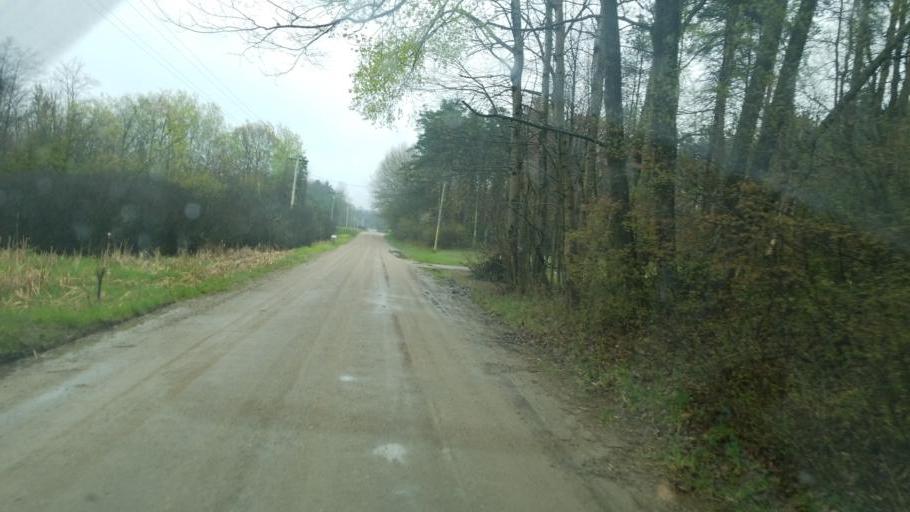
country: US
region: Michigan
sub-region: Montcalm County
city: Lakeview
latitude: 43.4678
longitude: -85.3027
